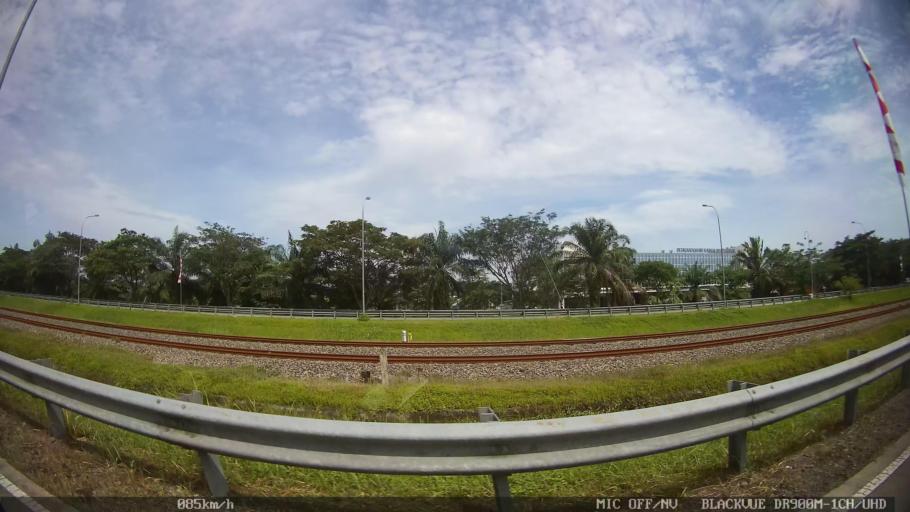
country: ID
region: North Sumatra
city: Percut
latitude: 3.6247
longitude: 98.8684
